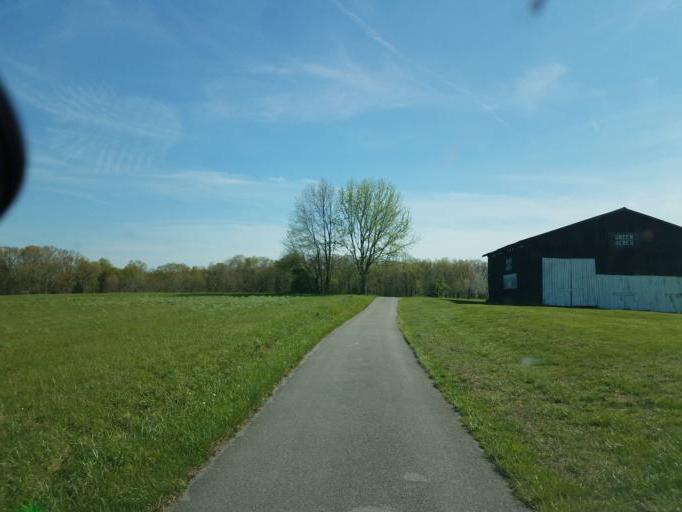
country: US
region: Kentucky
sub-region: Edmonson County
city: Brownsville
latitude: 37.1360
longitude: -86.1471
